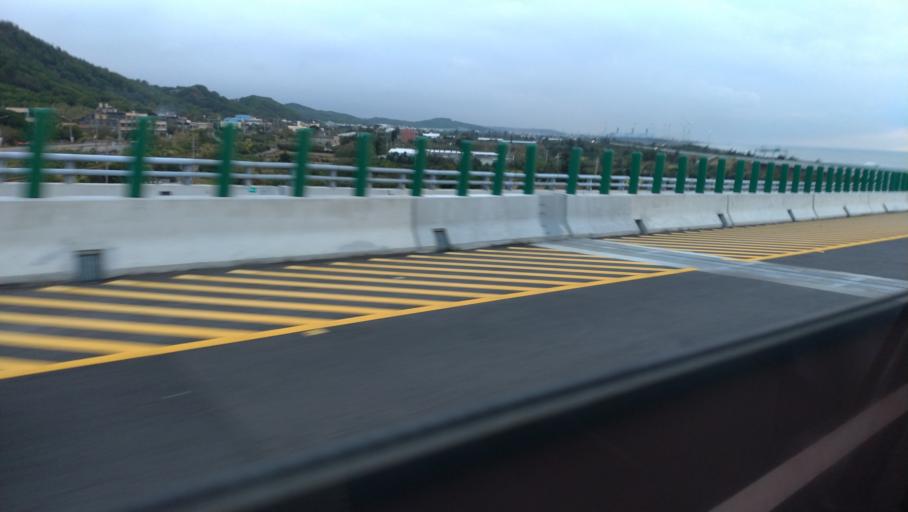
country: TW
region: Taiwan
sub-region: Miaoli
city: Miaoli
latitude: 24.5295
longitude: 120.6921
